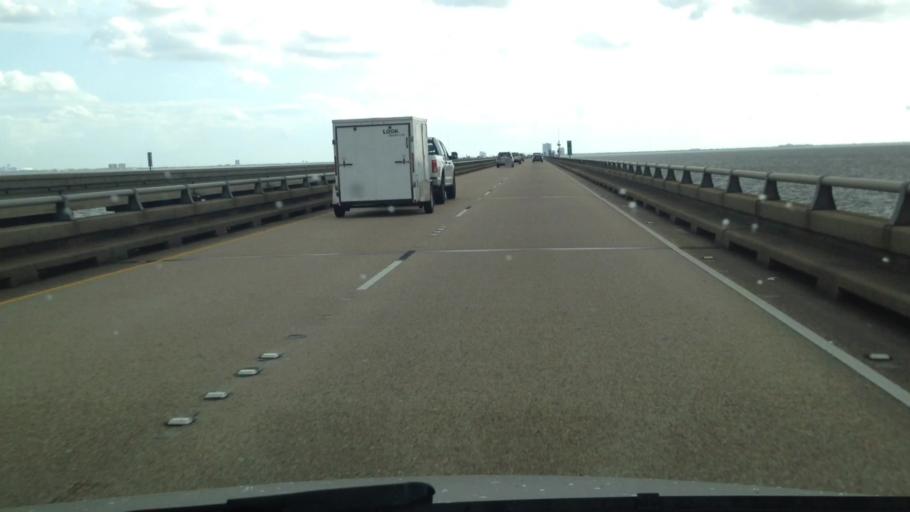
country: US
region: Louisiana
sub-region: Jefferson Parish
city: Metairie
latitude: 30.0987
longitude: -90.1407
